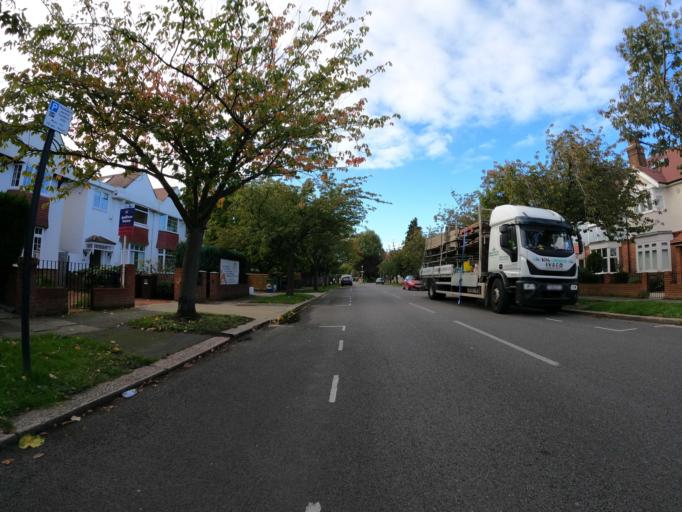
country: GB
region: England
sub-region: Greater London
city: Acton
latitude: 51.4844
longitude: -0.2679
